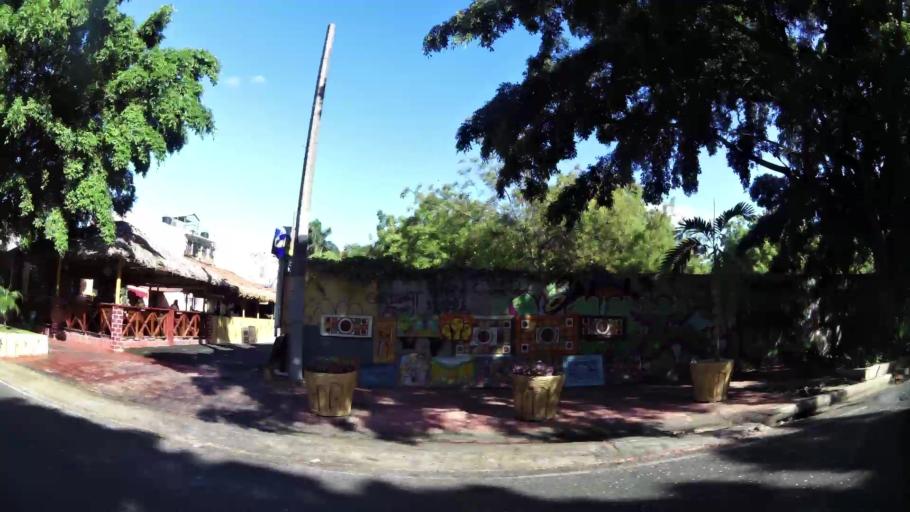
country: DO
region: Nacional
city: Ciudad Nueva
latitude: 18.4638
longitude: -69.9014
